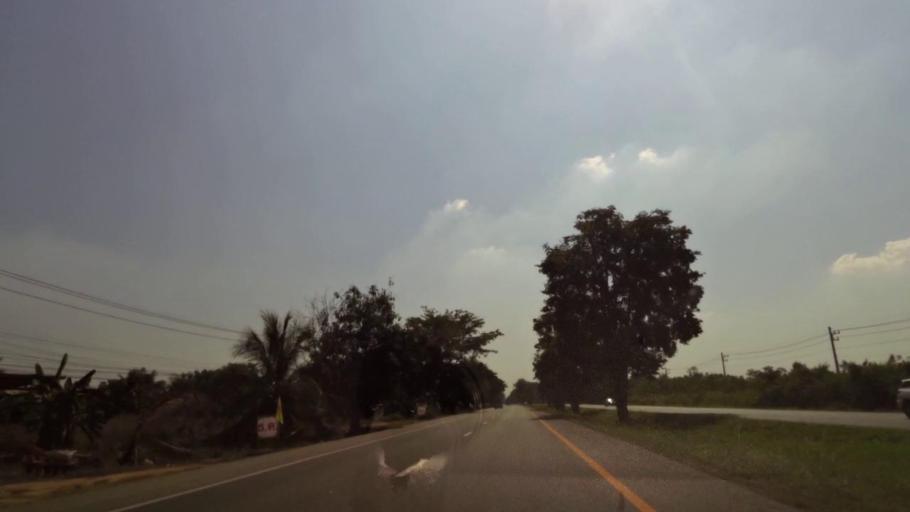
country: TH
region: Phichit
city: Bueng Na Rang
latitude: 16.2370
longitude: 100.1255
